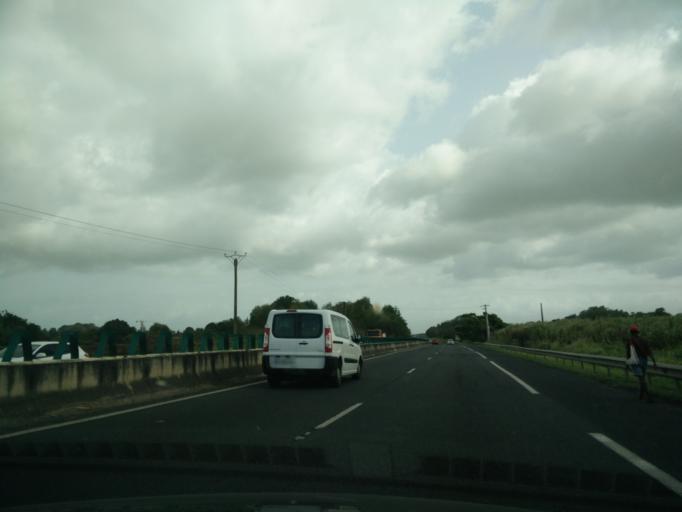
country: GP
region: Guadeloupe
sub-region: Guadeloupe
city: Les Abymes
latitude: 16.2913
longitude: -61.5031
